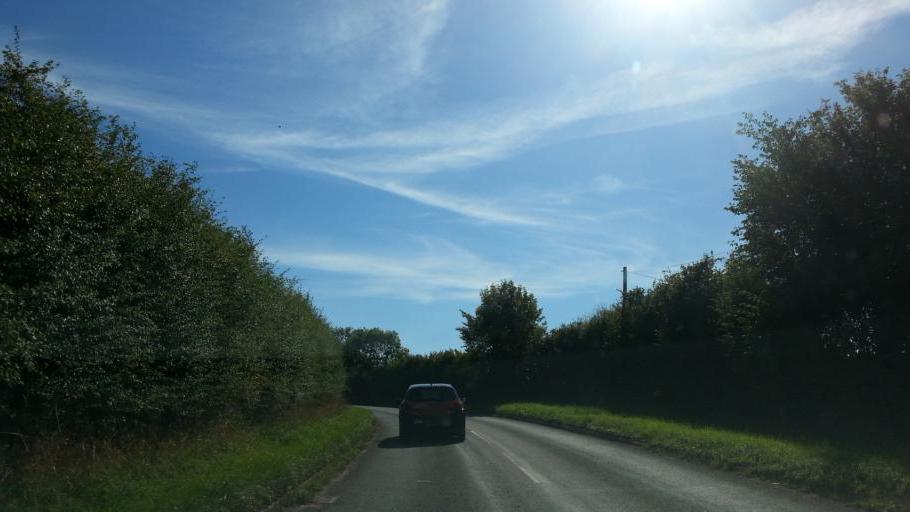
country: GB
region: England
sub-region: Staffordshire
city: Stafford
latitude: 52.7942
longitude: -2.1613
